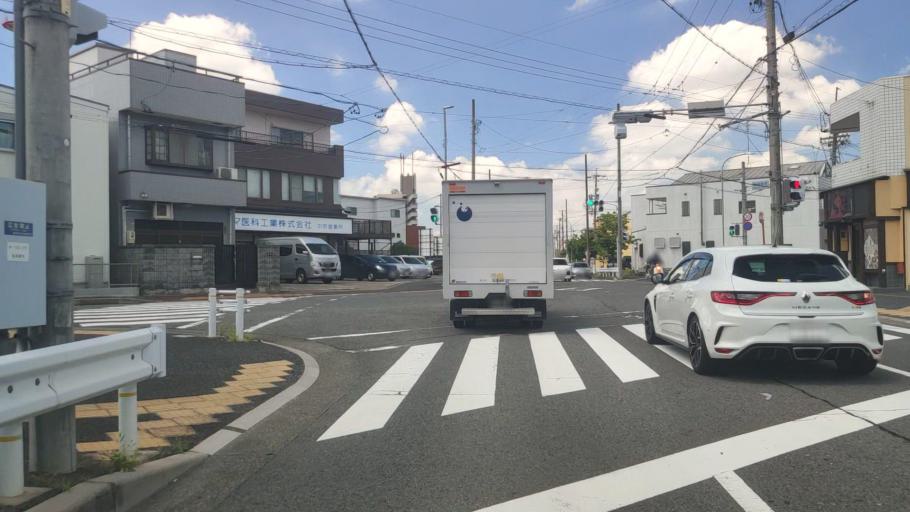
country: JP
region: Aichi
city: Nagoya-shi
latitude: 35.1528
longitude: 136.8627
